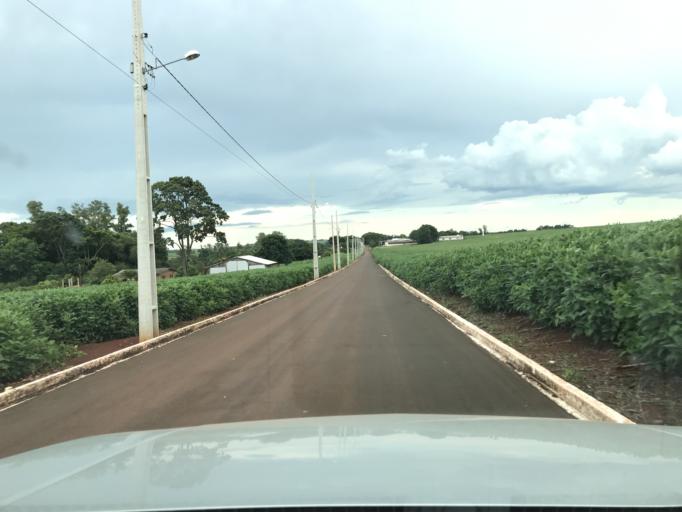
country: BR
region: Parana
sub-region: Palotina
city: Palotina
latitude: -24.2831
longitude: -53.7936
